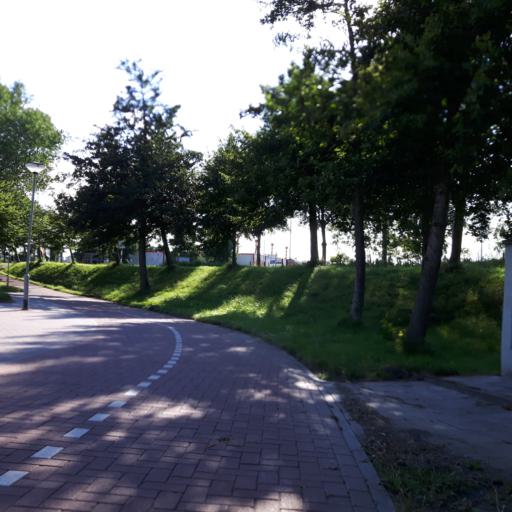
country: NL
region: Zeeland
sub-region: Gemeente Goes
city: Goes
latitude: 51.5106
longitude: 3.8948
